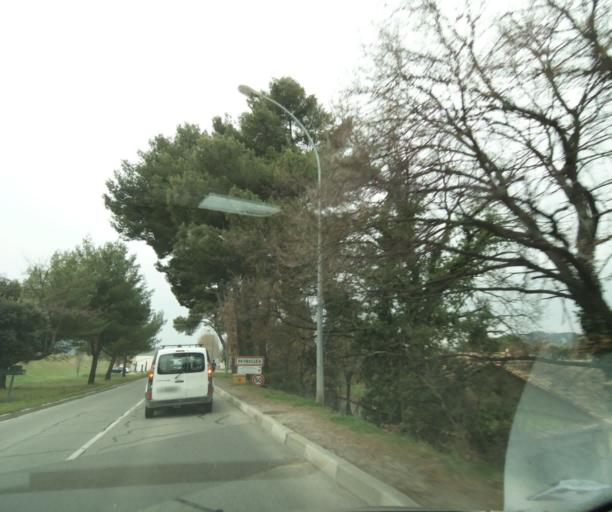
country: FR
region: Provence-Alpes-Cote d'Azur
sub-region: Departement des Bouches-du-Rhone
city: Peyrolles-en-Provence
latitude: 43.6452
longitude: 5.6001
